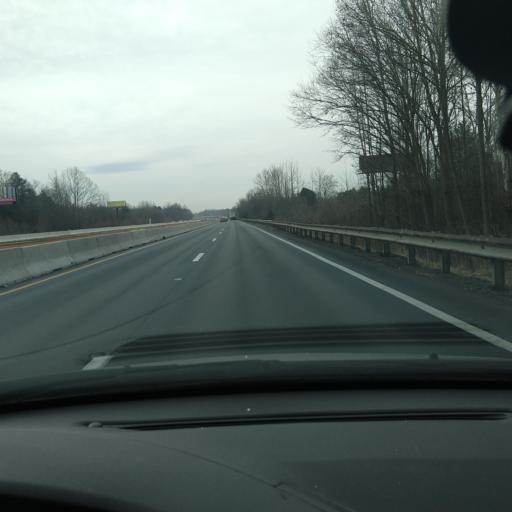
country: US
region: North Carolina
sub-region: Rowan County
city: China Grove
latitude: 35.5513
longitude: -80.5714
